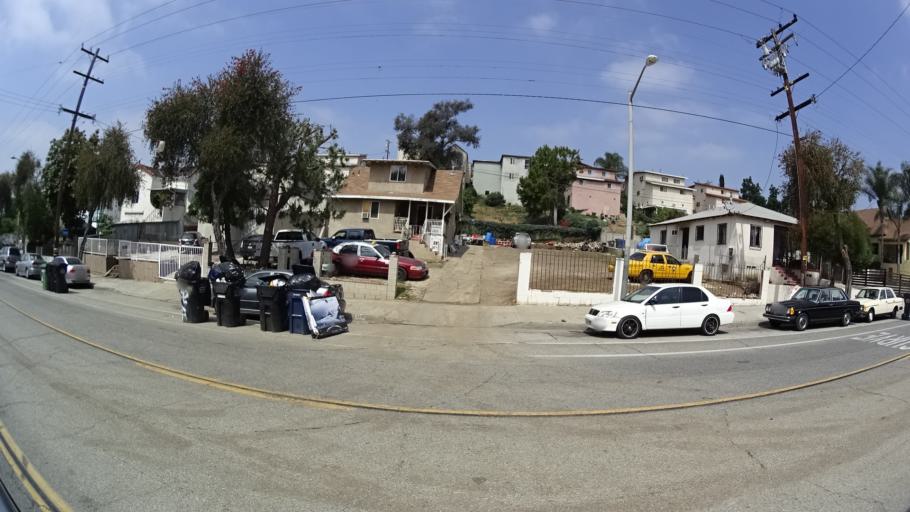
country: US
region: California
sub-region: Los Angeles County
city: Belvedere
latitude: 34.0498
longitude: -118.1889
